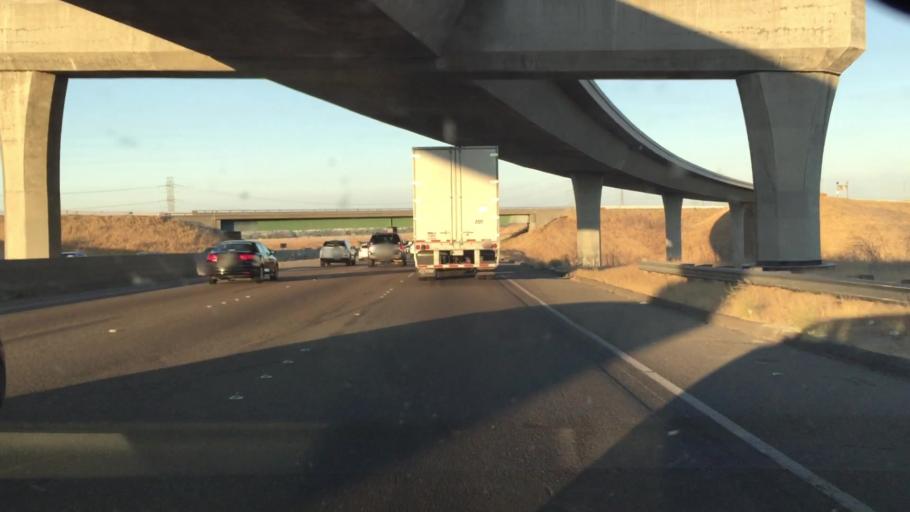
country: US
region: California
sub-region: San Joaquin County
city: Mountain House
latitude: 37.7424
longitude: -121.5631
